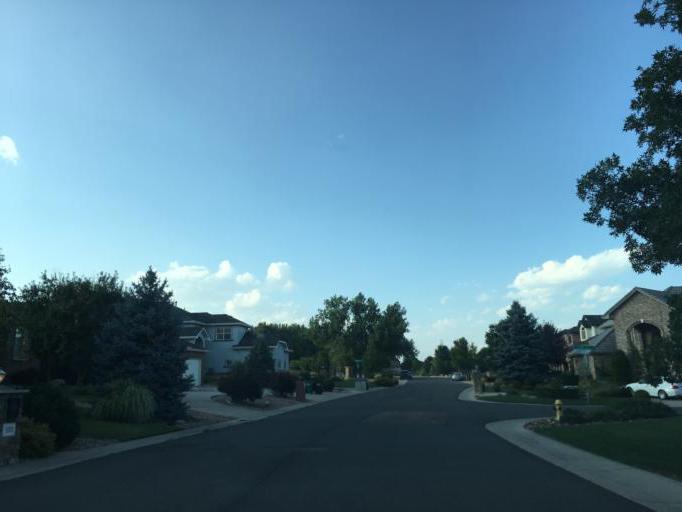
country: US
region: Colorado
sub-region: Jefferson County
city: Applewood
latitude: 39.7930
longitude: -105.1694
